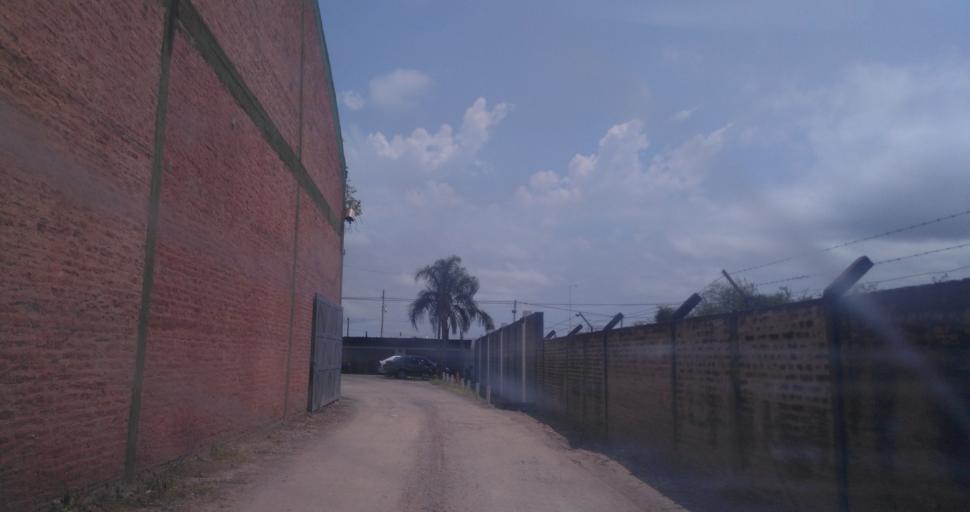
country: AR
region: Chaco
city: Fontana
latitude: -27.4619
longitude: -59.0393
